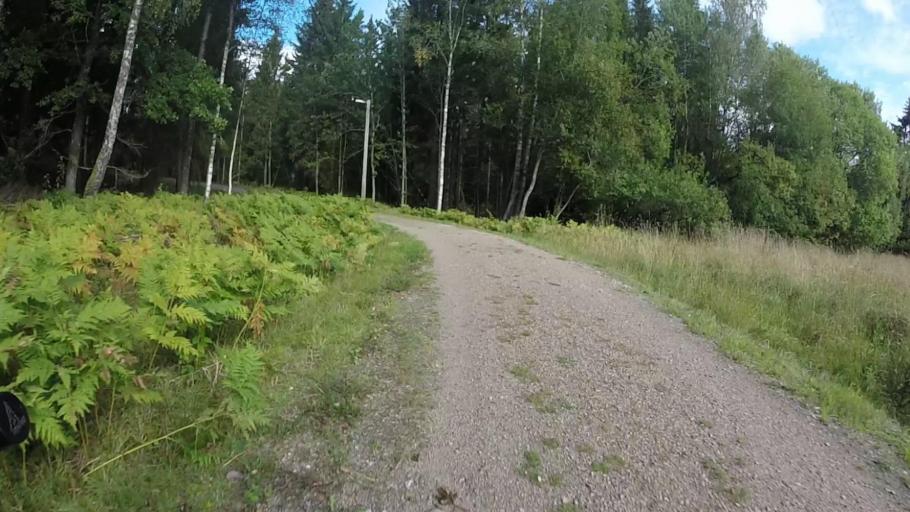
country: SE
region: Vaestra Goetaland
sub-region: Trollhattan
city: Trollhattan
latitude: 58.2517
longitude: 12.2473
